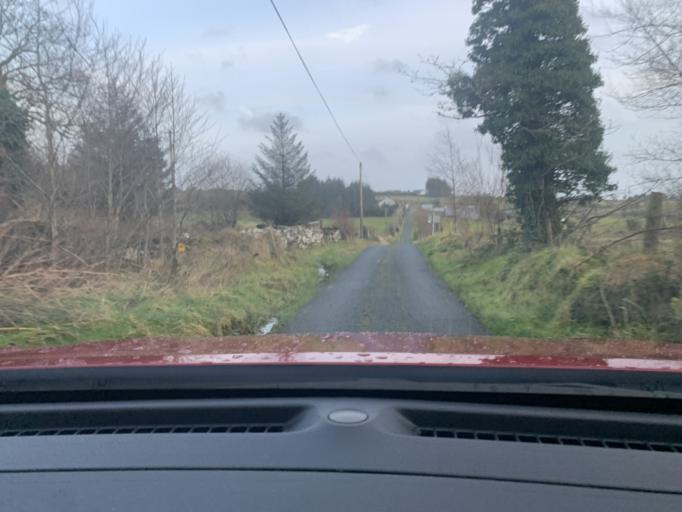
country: IE
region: Connaught
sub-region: Roscommon
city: Ballaghaderreen
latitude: 53.9506
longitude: -8.5186
